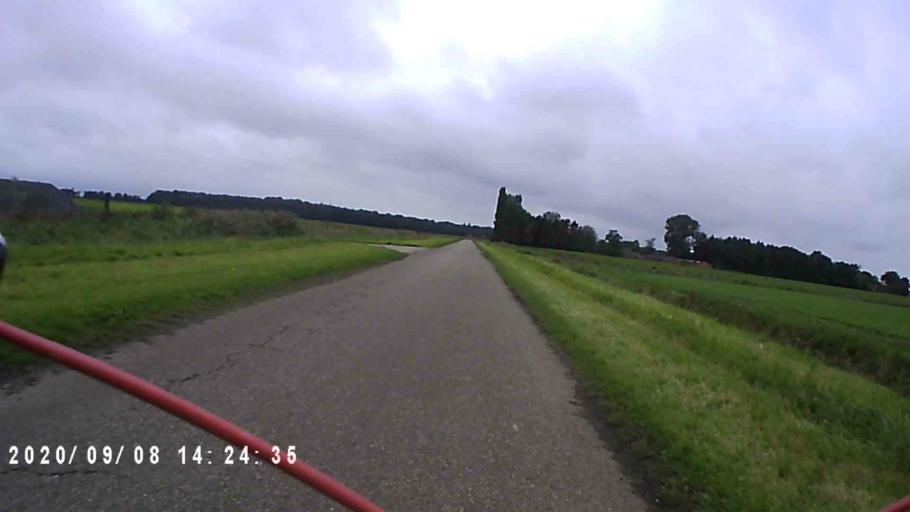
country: NL
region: Groningen
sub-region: Gemeente Slochteren
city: Slochteren
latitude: 53.2189
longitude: 6.8311
